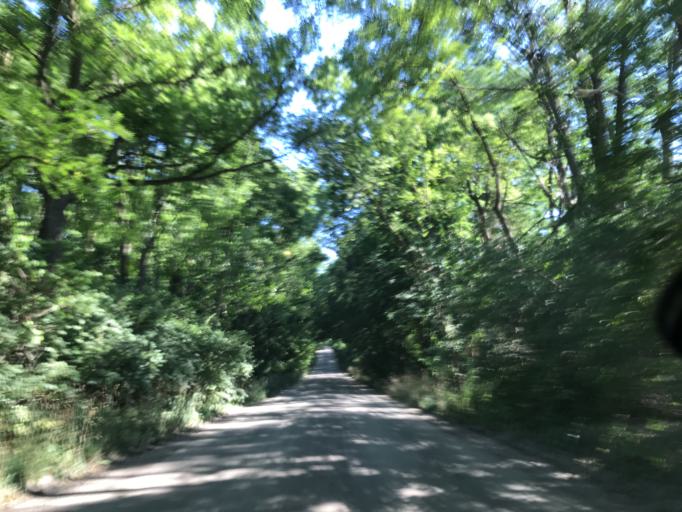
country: US
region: Michigan
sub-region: Washtenaw County
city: Ypsilanti
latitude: 42.2914
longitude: -83.6531
